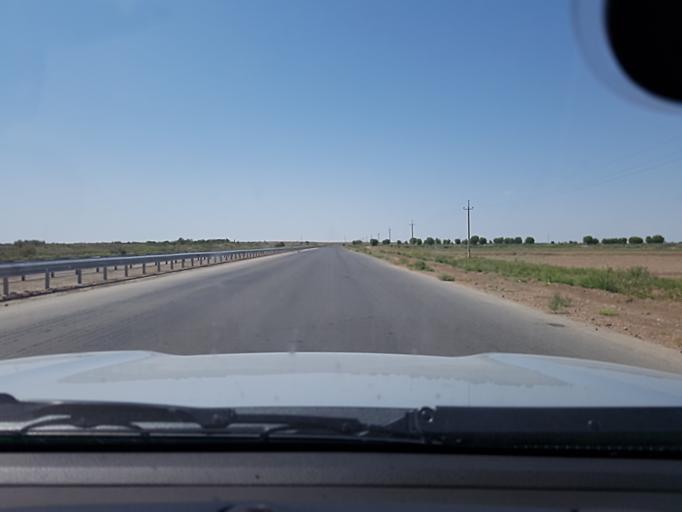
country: TM
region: Dasoguz
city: Yylanly
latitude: 41.7536
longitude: 59.3984
